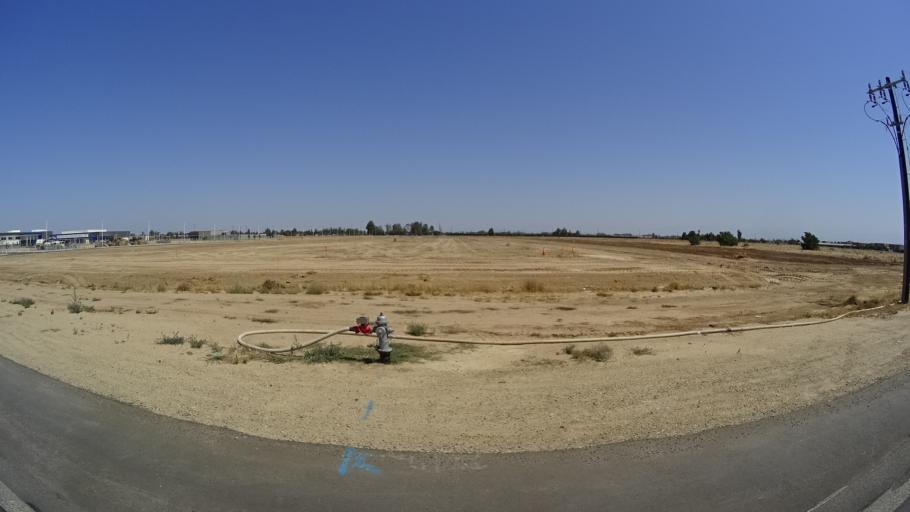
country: US
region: California
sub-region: Fresno County
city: Sunnyside
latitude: 36.7075
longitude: -119.6774
